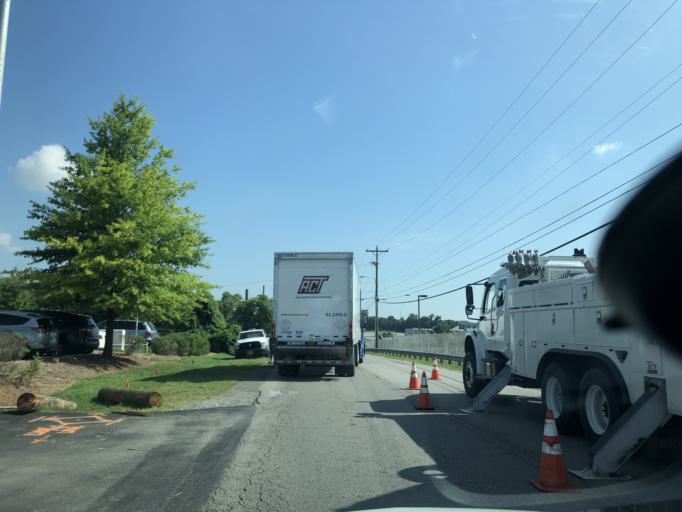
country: US
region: Tennessee
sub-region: Rutherford County
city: La Vergne
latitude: 36.0196
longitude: -86.6069
